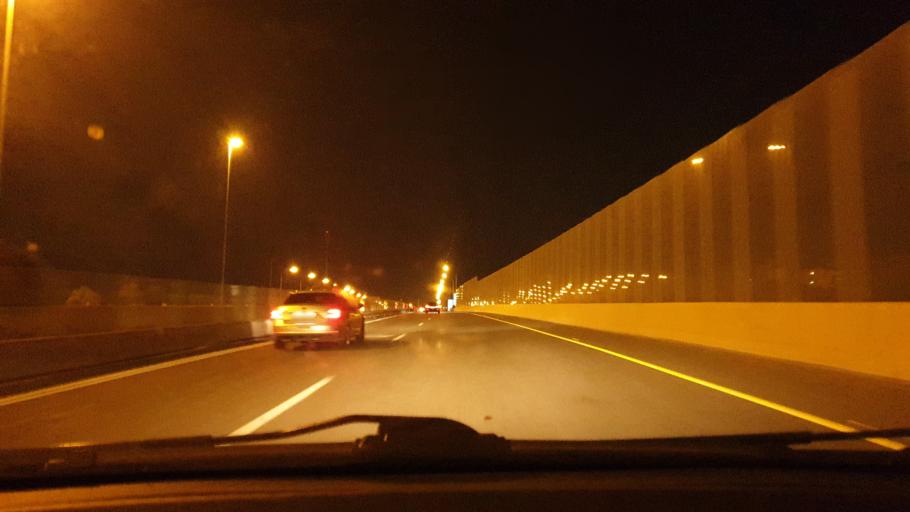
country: IL
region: Central District
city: Ramla
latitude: 31.9186
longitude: 34.8581
